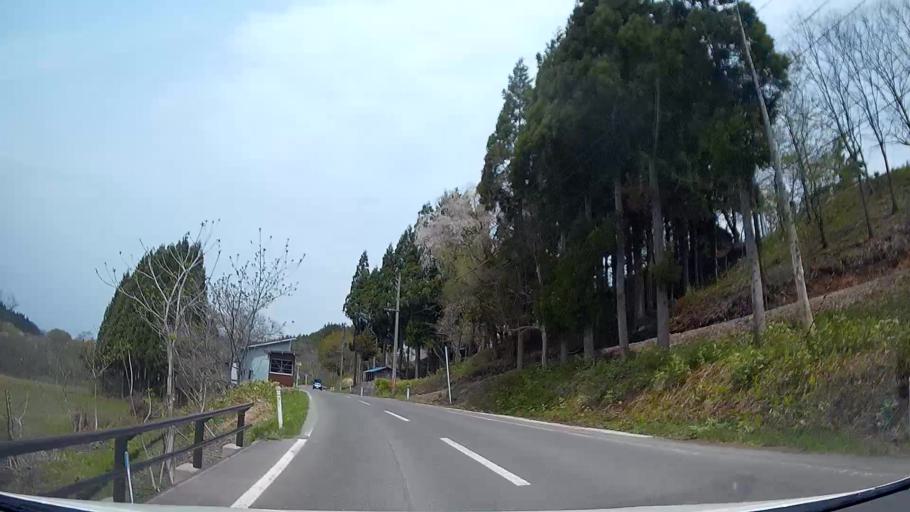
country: JP
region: Akita
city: Hanawa
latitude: 40.0386
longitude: 140.8230
